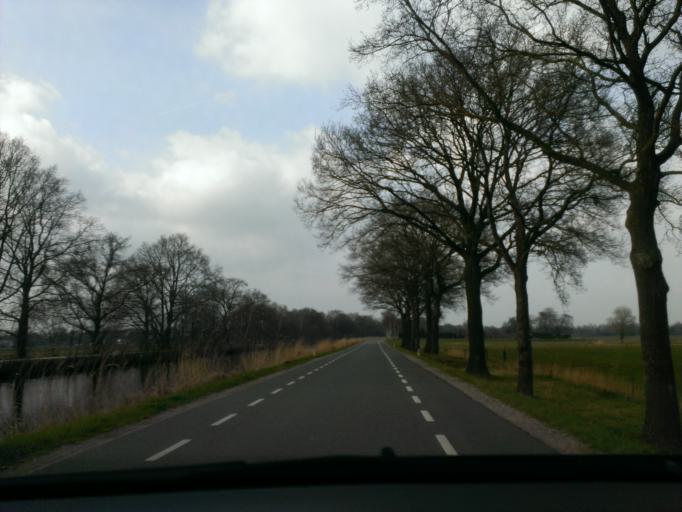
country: NL
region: Gelderland
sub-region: Gemeente Epe
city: Oene
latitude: 52.3512
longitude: 6.0244
